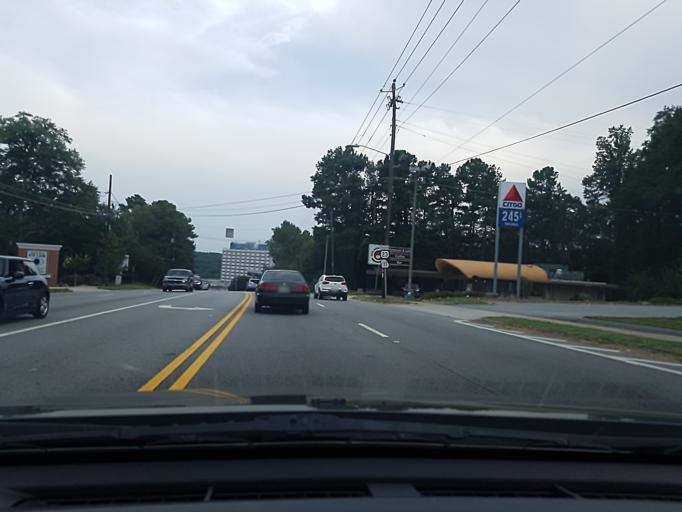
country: US
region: Georgia
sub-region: DeKalb County
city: North Druid Hills
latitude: 33.8067
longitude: -84.3104
